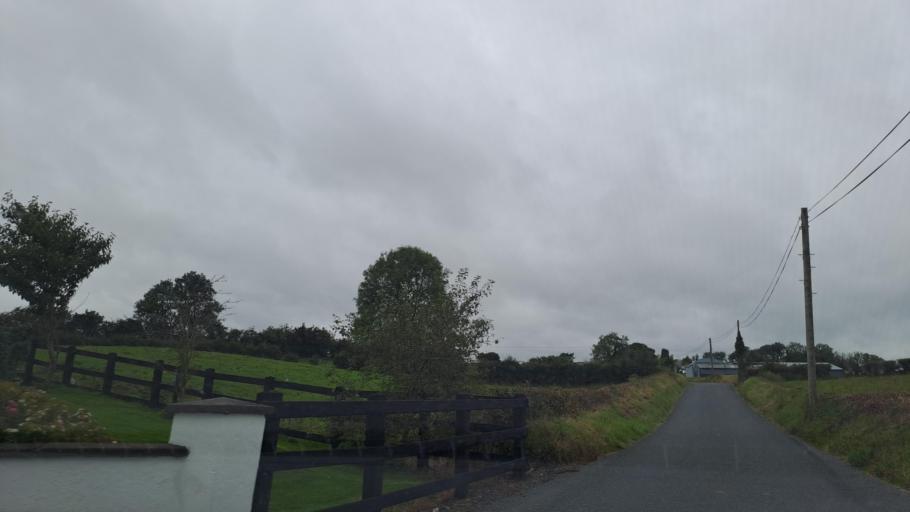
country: IE
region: Ulster
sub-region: An Cabhan
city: Kingscourt
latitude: 54.0087
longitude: -6.8736
